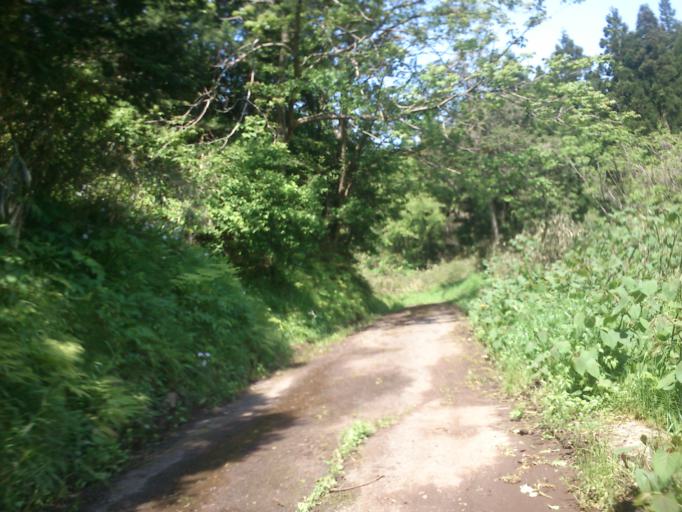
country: JP
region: Kyoto
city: Miyazu
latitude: 35.7130
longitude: 135.1429
